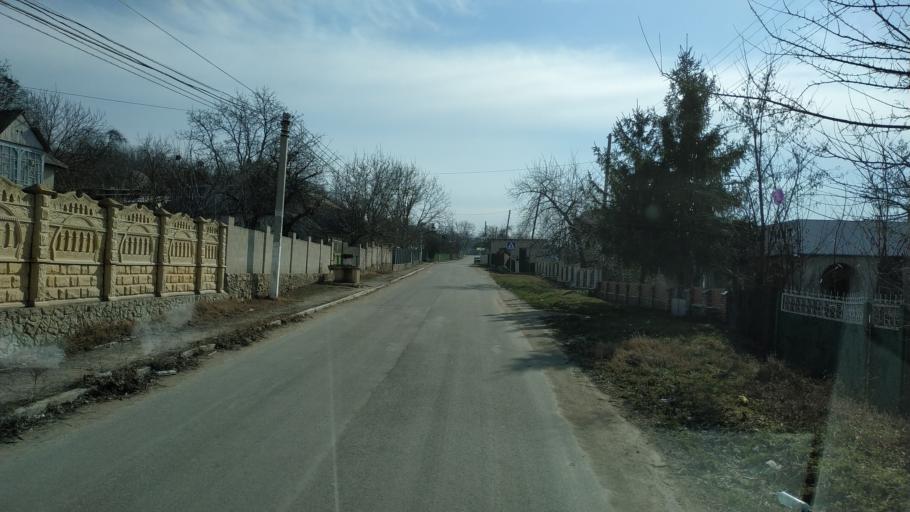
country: MD
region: Nisporeni
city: Nisporeni
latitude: 47.1761
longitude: 28.1255
